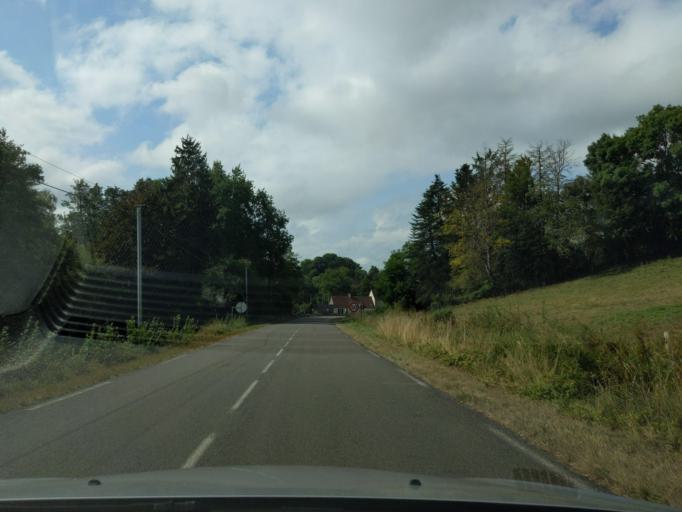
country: FR
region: Bourgogne
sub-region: Departement de Saone-et-Loire
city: Bourbon-Lancy
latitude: 46.6957
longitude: 3.8623
